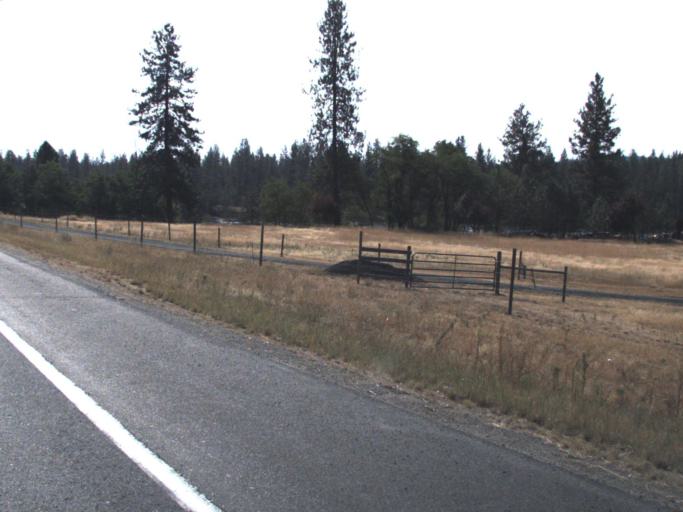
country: US
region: Washington
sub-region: Spokane County
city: Fairwood
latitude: 47.7594
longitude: -117.5324
